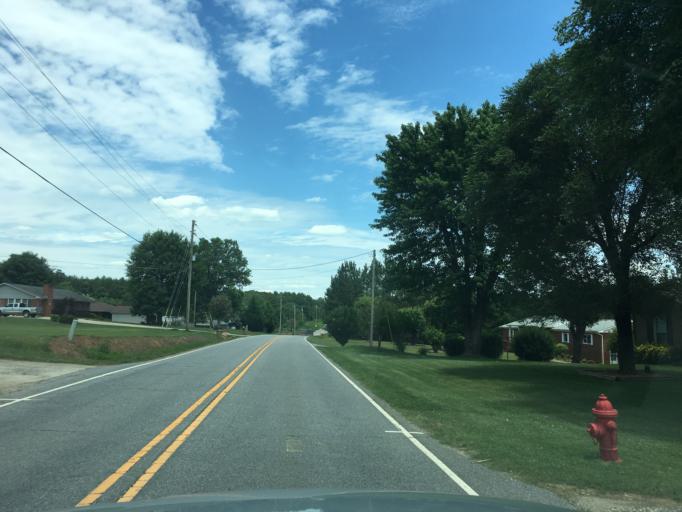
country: US
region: North Carolina
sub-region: Burke County
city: Glen Alpine
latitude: 35.6806
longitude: -81.7694
